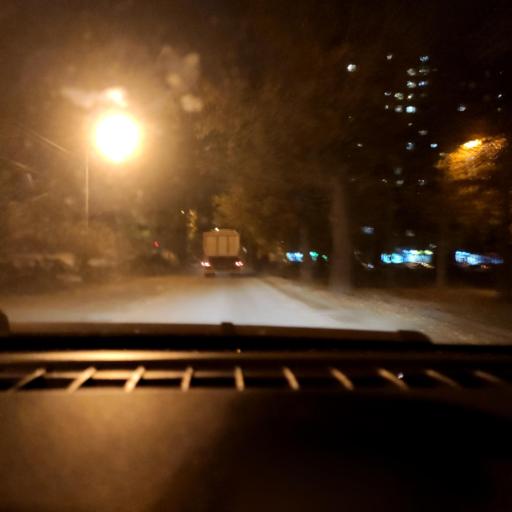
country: RU
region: Voronezj
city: Maslovka
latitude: 51.6376
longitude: 39.2737
